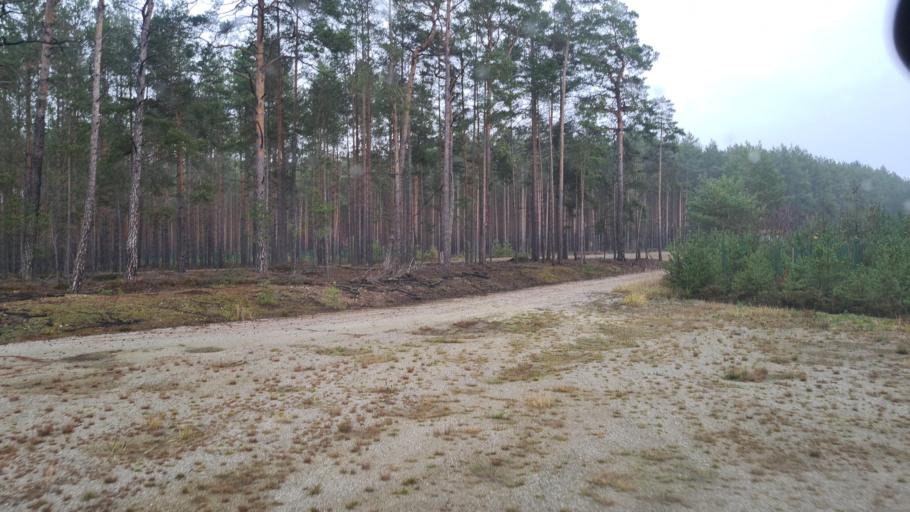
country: DE
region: Brandenburg
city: Sallgast
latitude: 51.6411
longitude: 13.8226
